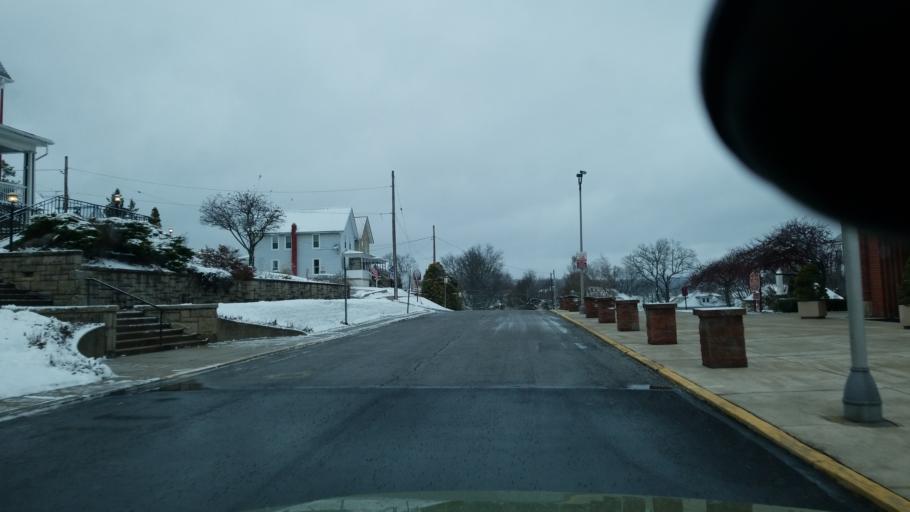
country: US
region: Pennsylvania
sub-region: Clearfield County
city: DuBois
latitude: 41.1202
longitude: -78.7701
